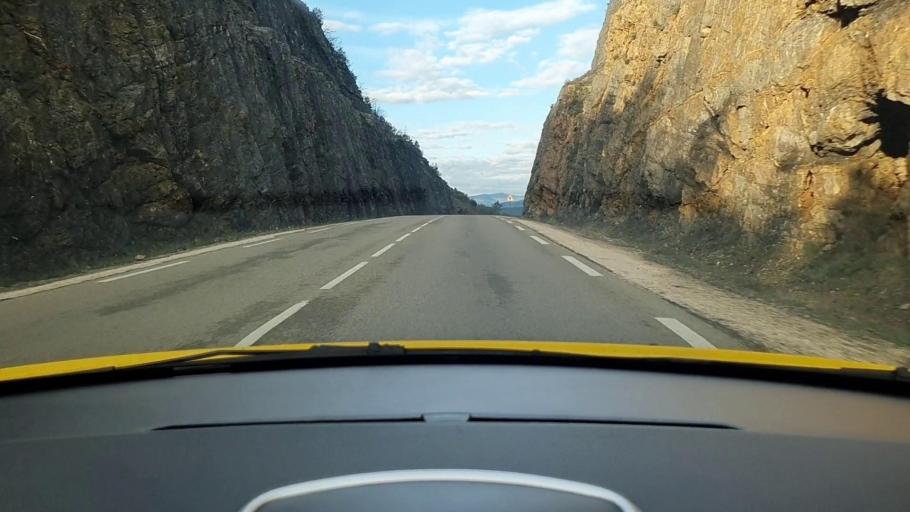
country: FR
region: Languedoc-Roussillon
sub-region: Departement du Gard
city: Laval-Pradel
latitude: 44.2135
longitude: 4.0911
